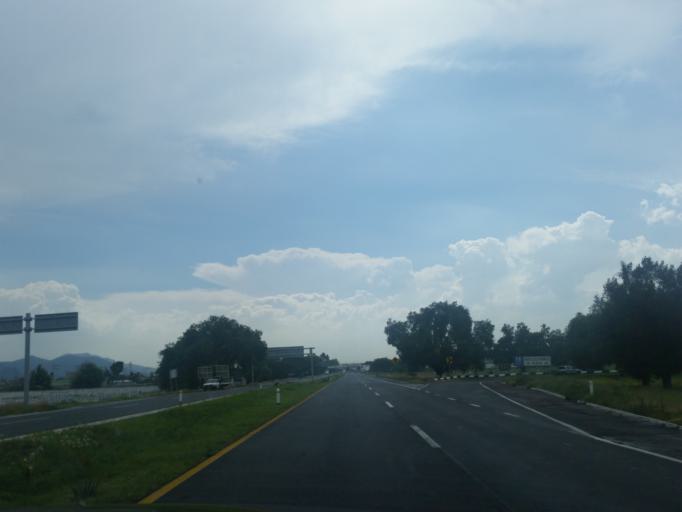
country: MX
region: Mexico
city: Acolman
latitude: 19.6186
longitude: -98.9495
